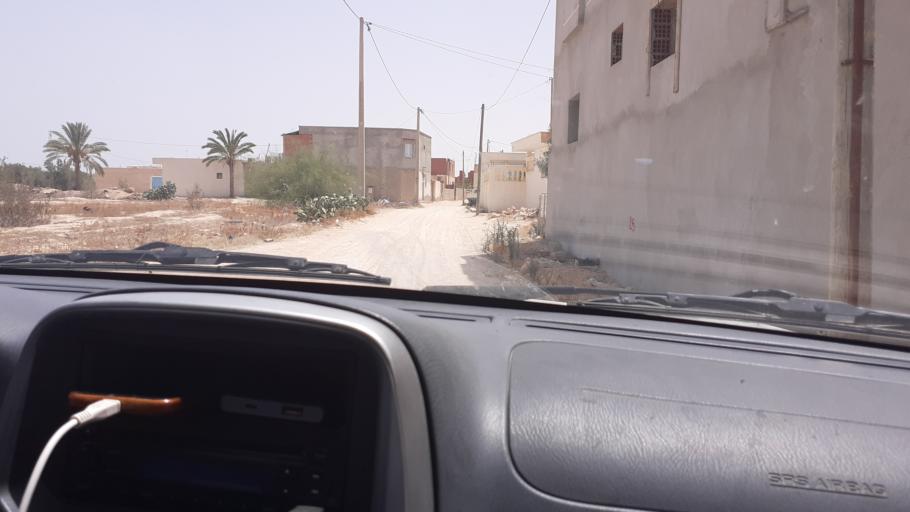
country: TN
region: Qabis
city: Matmata
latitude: 33.6090
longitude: 10.2870
